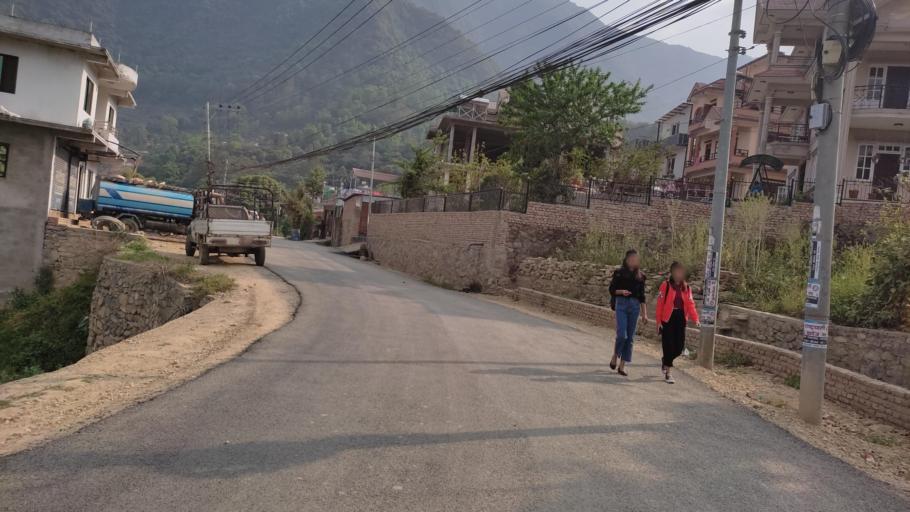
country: NP
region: Central Region
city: Kirtipur
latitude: 27.6651
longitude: 85.2584
